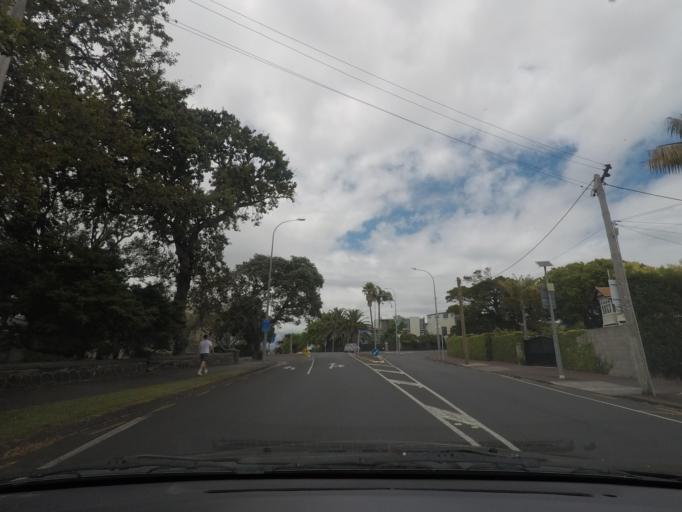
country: NZ
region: Auckland
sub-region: Auckland
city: Auckland
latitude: -36.8561
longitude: 174.7872
